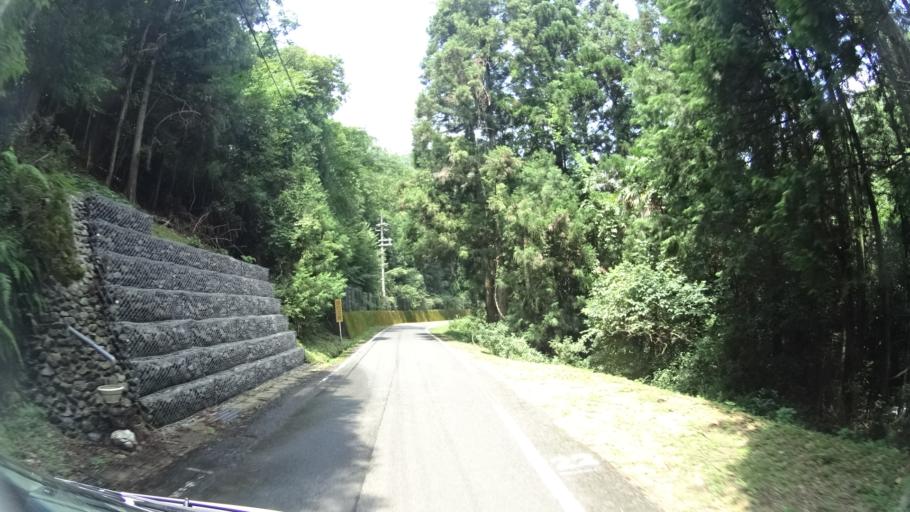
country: JP
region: Hyogo
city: Sasayama
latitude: 35.1837
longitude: 135.2163
